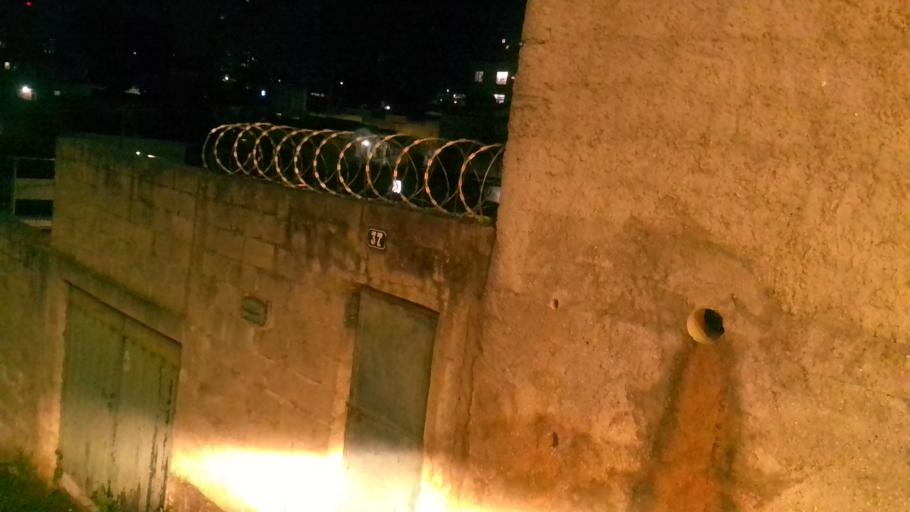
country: BR
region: Minas Gerais
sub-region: Belo Horizonte
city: Belo Horizonte
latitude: -19.9020
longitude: -43.9574
